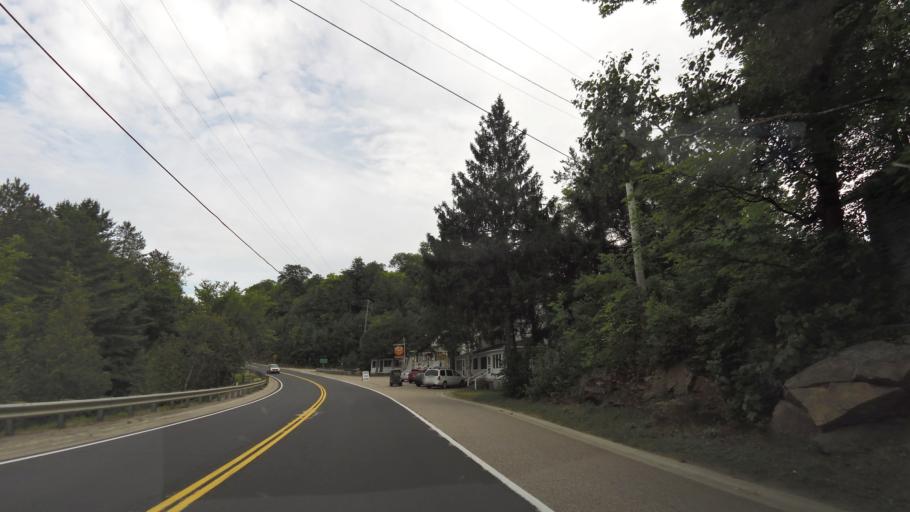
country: CA
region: Ontario
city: Omemee
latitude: 44.8200
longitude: -78.7768
